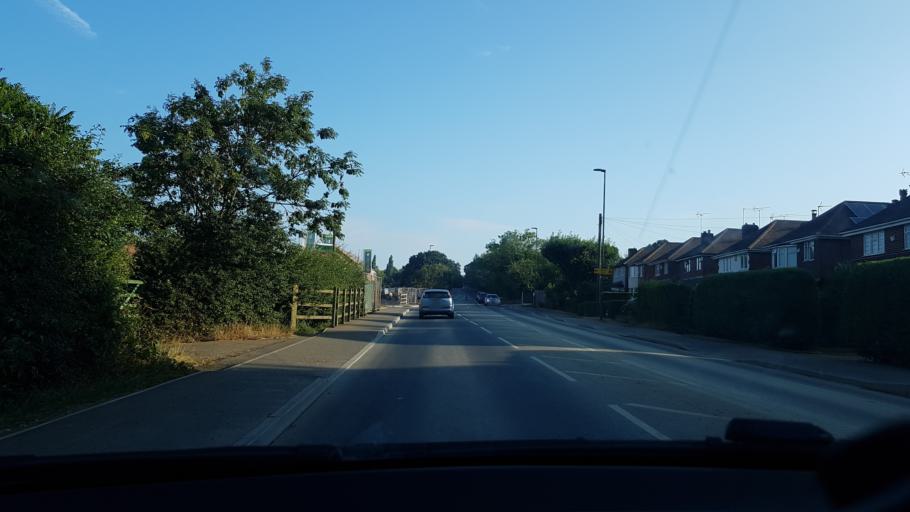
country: GB
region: England
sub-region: Derbyshire
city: Ilkeston
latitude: 52.9539
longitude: -1.3072
